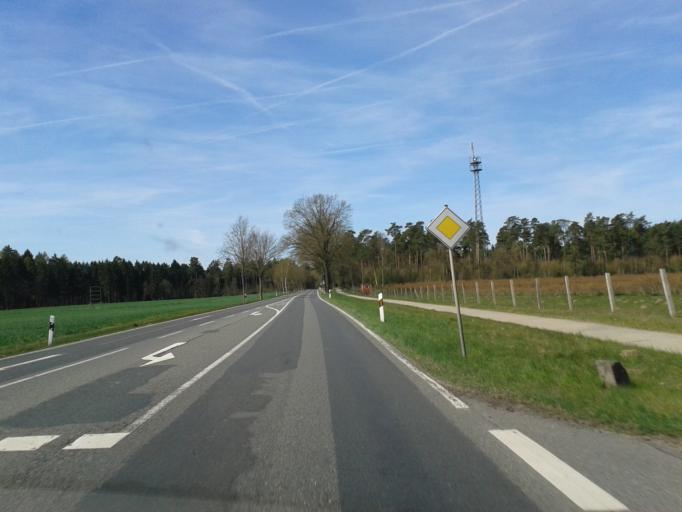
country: DE
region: Lower Saxony
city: Eimke
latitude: 52.9674
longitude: 10.3577
